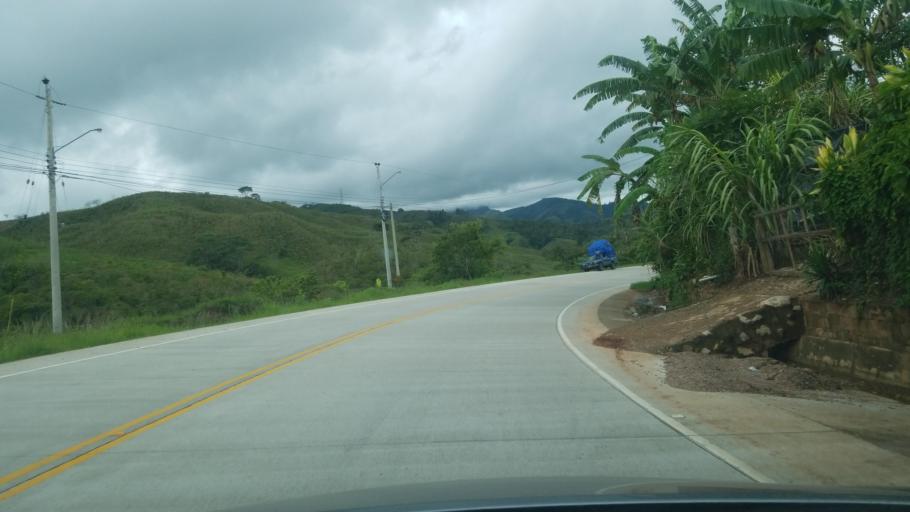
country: HN
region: Copan
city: San Jeronimo
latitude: 14.9408
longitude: -88.9157
